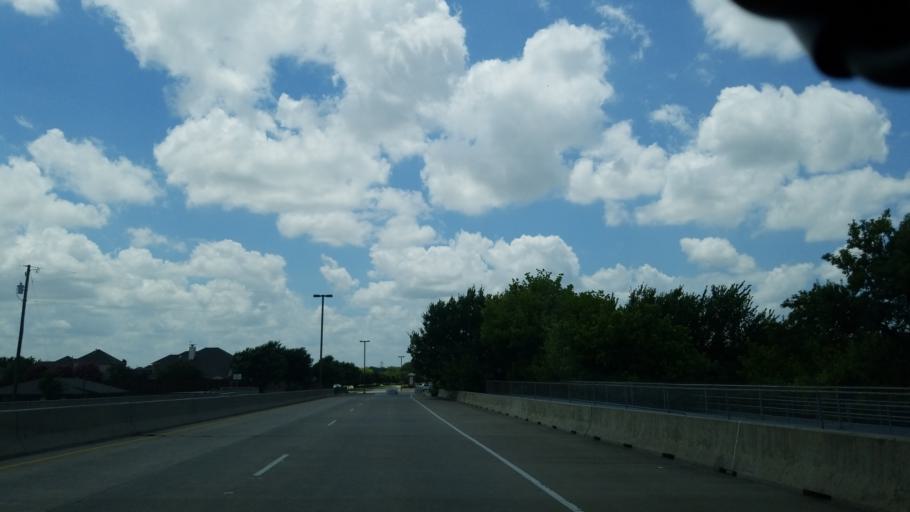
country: US
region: Texas
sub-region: Dallas County
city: Carrollton
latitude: 32.9661
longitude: -96.9442
